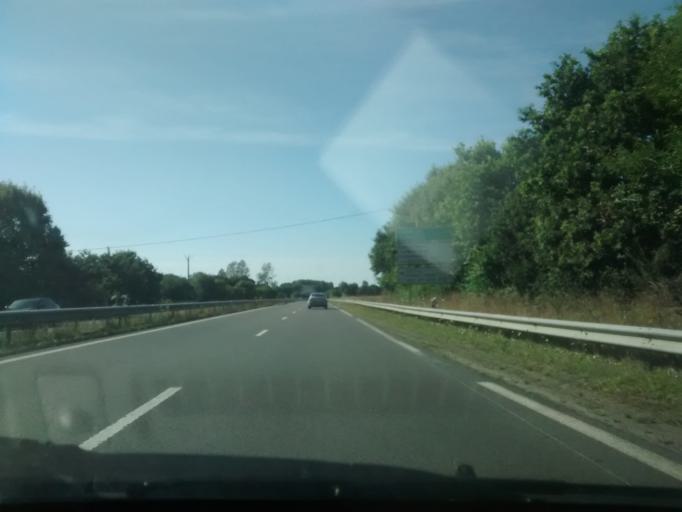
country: FR
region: Brittany
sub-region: Departement des Cotes-d'Armor
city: Cavan
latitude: 48.6625
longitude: -3.3416
